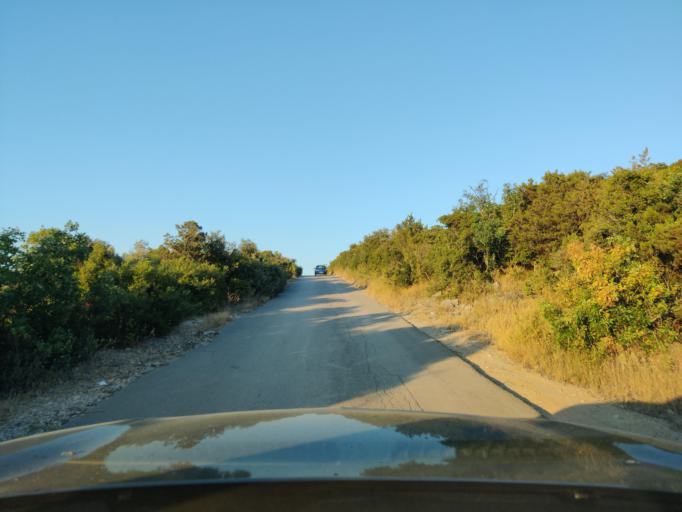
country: HR
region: Sibensko-Kniniska
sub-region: Grad Sibenik
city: Tisno
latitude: 43.8093
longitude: 15.6349
